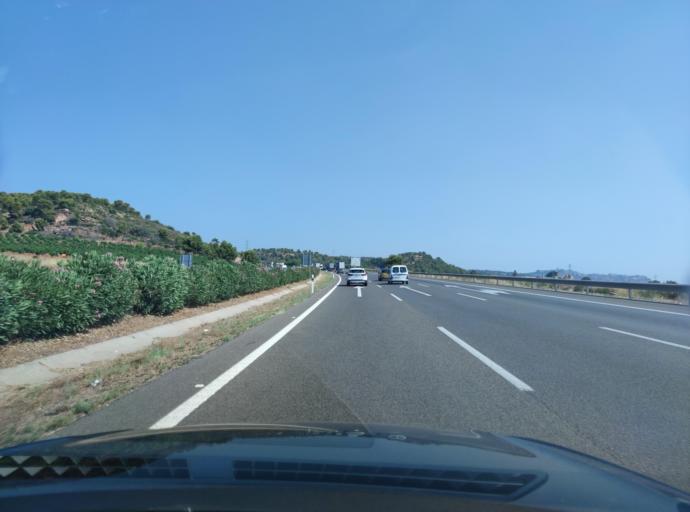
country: ES
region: Valencia
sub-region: Provincia de Valencia
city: Pucol
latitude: 39.6443
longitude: -0.3002
